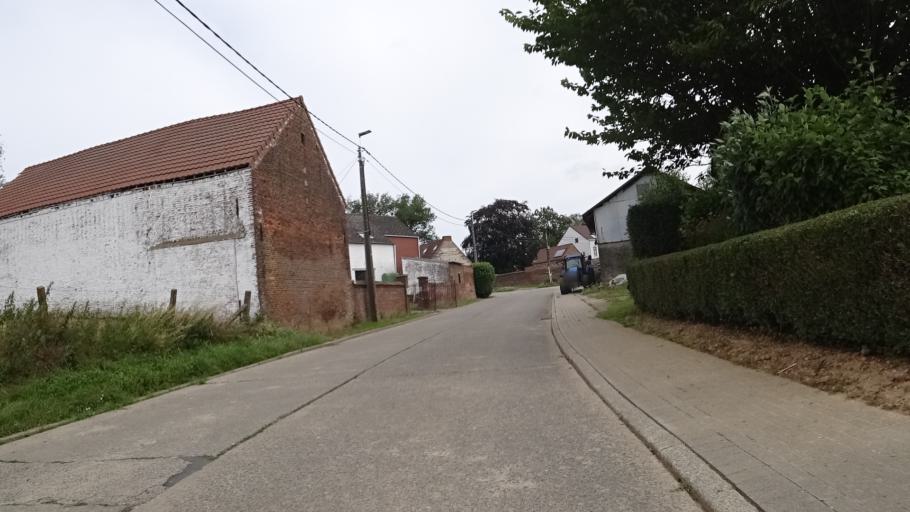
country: BE
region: Wallonia
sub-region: Province du Brabant Wallon
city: Walhain-Saint-Paul
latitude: 50.6444
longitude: 4.6726
